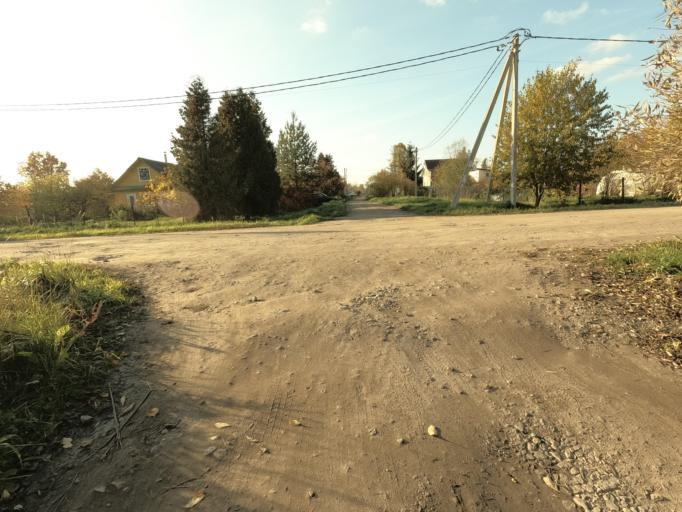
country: RU
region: Leningrad
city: Mga
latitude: 59.7533
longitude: 31.0537
